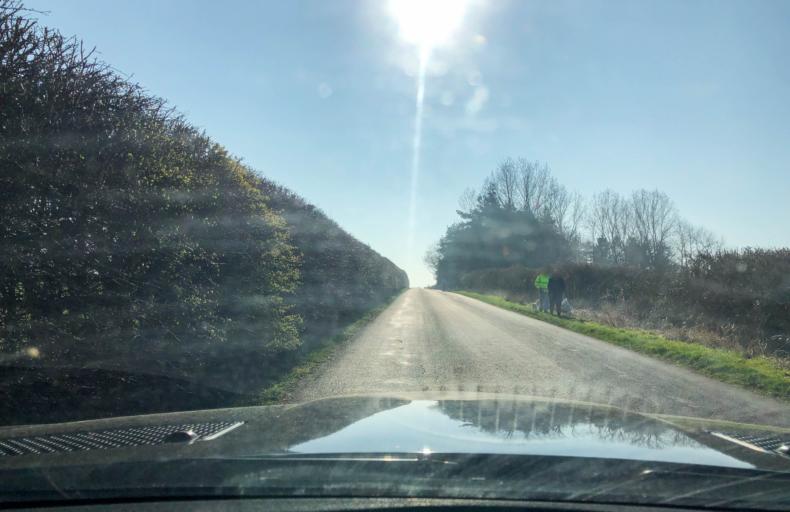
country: GB
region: England
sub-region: Warwickshire
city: Wellesbourne Mountford
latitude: 52.1872
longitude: -1.5402
